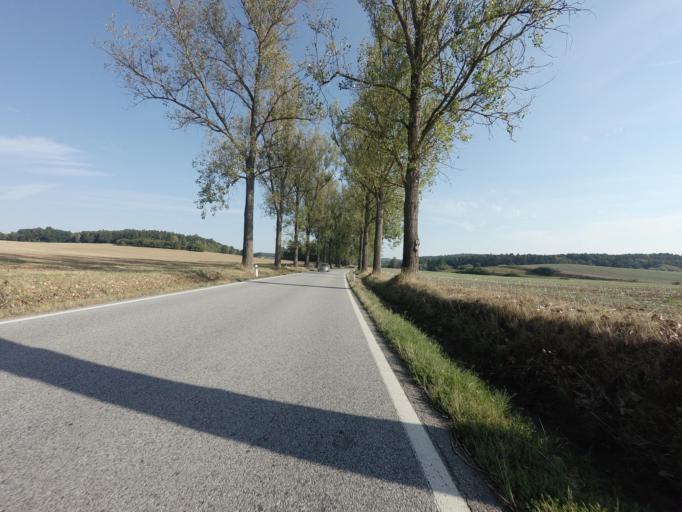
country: CZ
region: Jihocesky
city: Tyn nad Vltavou
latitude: 49.2359
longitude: 14.4206
